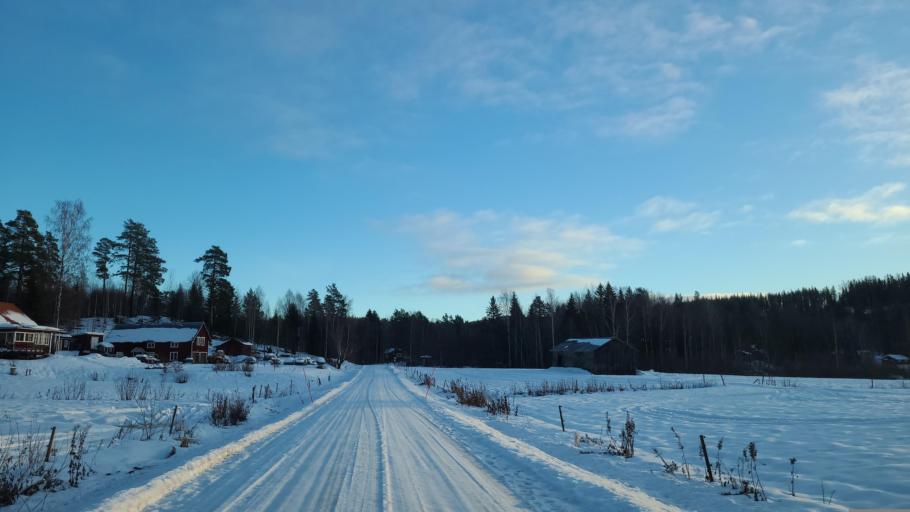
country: SE
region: Gaevleborg
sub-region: Bollnas Kommun
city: Kilafors
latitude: 61.3948
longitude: 16.6856
